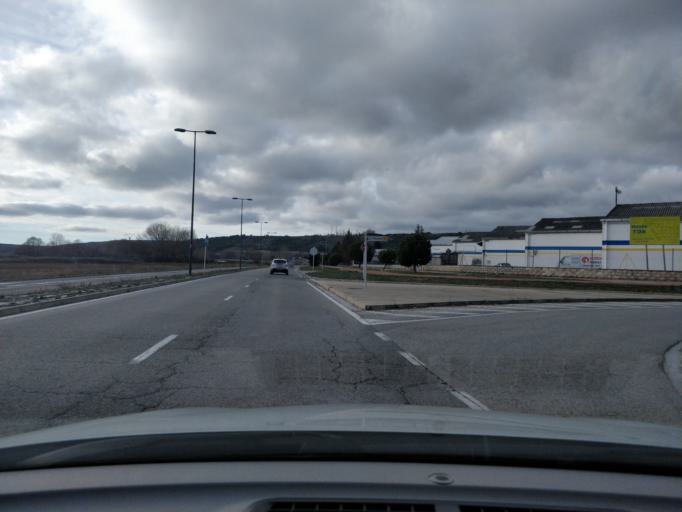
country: ES
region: Castille and Leon
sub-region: Provincia de Burgos
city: Villalbilla de Burgos
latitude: 42.3578
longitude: -3.7623
